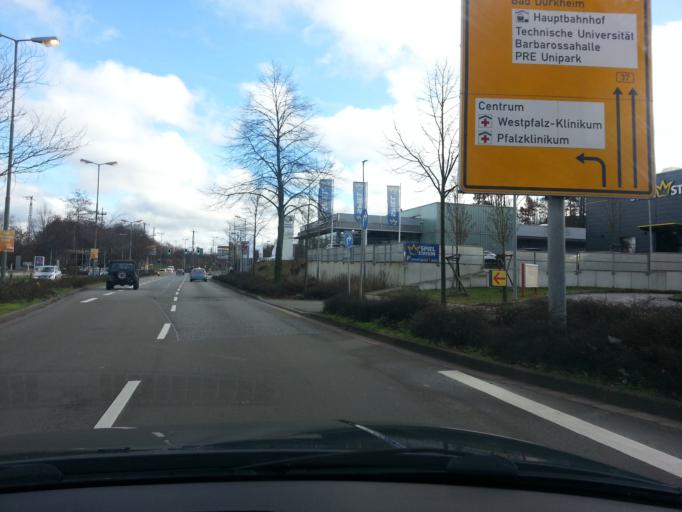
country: DE
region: Rheinland-Pfalz
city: Kaiserslautern
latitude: 49.4336
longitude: 7.7495
